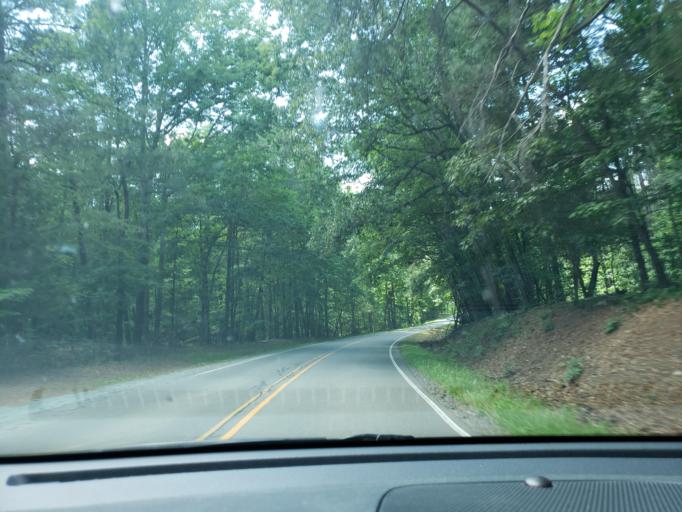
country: US
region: North Carolina
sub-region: Orange County
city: Chapel Hill
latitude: 35.9997
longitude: -79.0237
